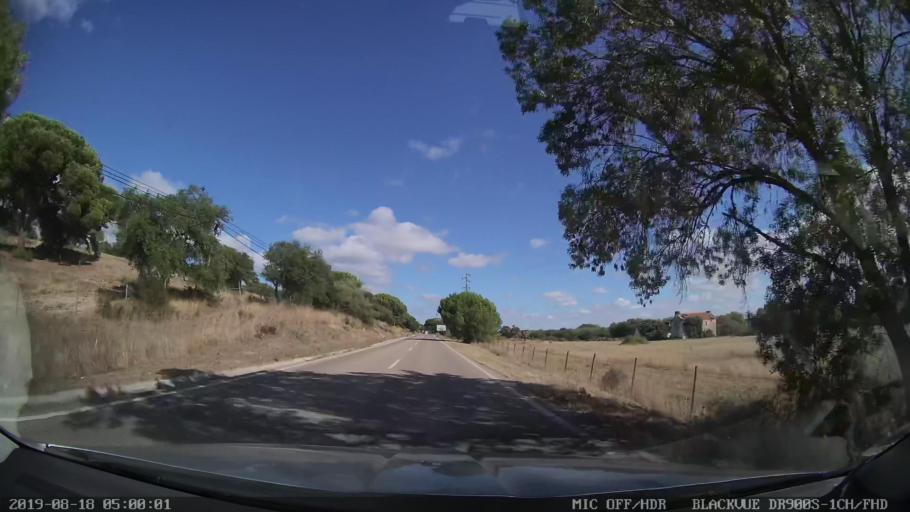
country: PT
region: Santarem
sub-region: Benavente
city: Poceirao
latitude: 38.8521
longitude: -8.7223
